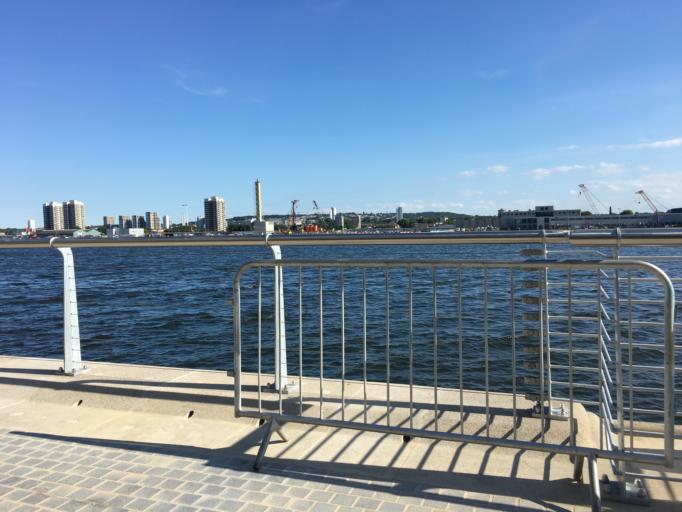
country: GB
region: England
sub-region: Greater London
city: Woolwich
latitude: 51.5073
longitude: 0.0522
